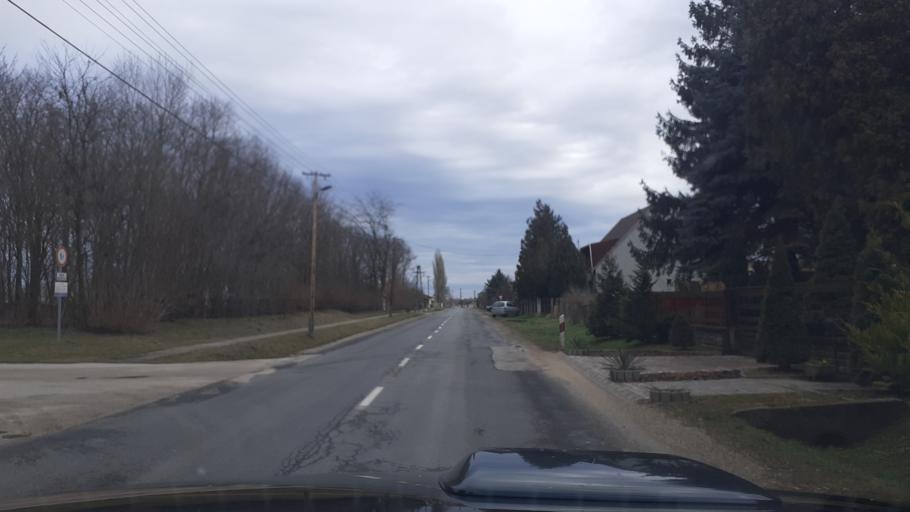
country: HU
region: Fejer
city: Sarosd
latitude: 47.0396
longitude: 18.6533
